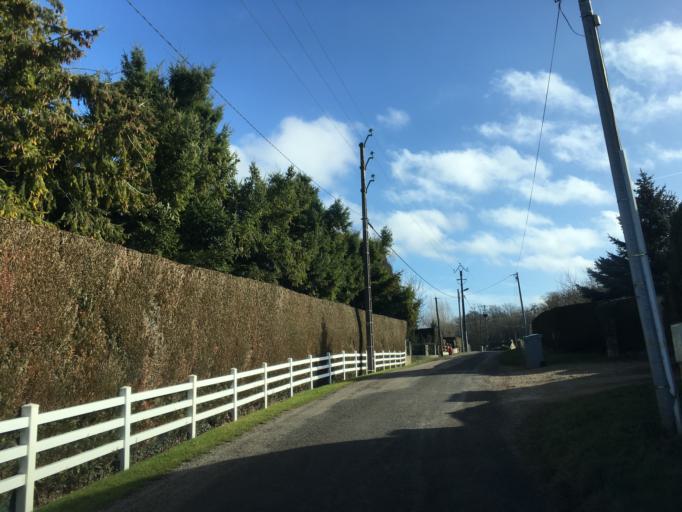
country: FR
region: Haute-Normandie
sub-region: Departement de l'Eure
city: La Chapelle-Reanville
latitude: 49.1218
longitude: 1.3993
